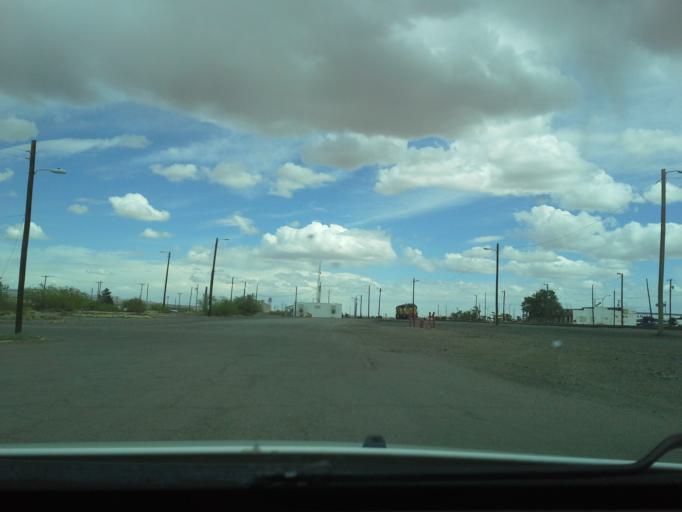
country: US
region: New Mexico
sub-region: Hidalgo County
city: Lordsburg
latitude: 32.3505
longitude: -108.7065
